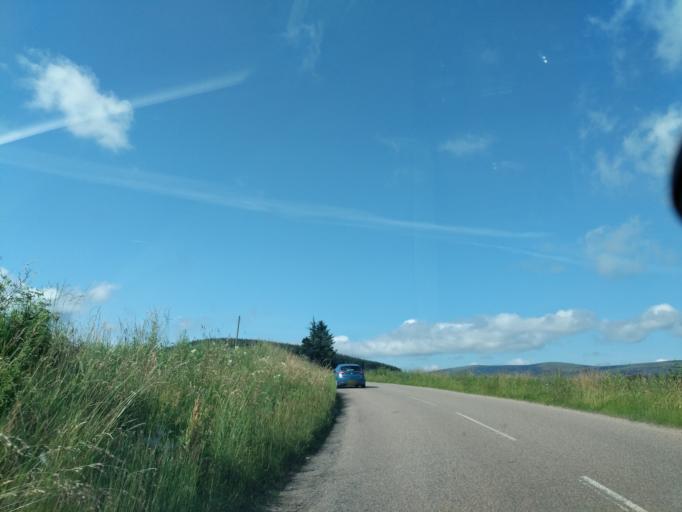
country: GB
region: Scotland
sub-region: Moray
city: Dufftown
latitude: 57.3518
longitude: -3.3009
